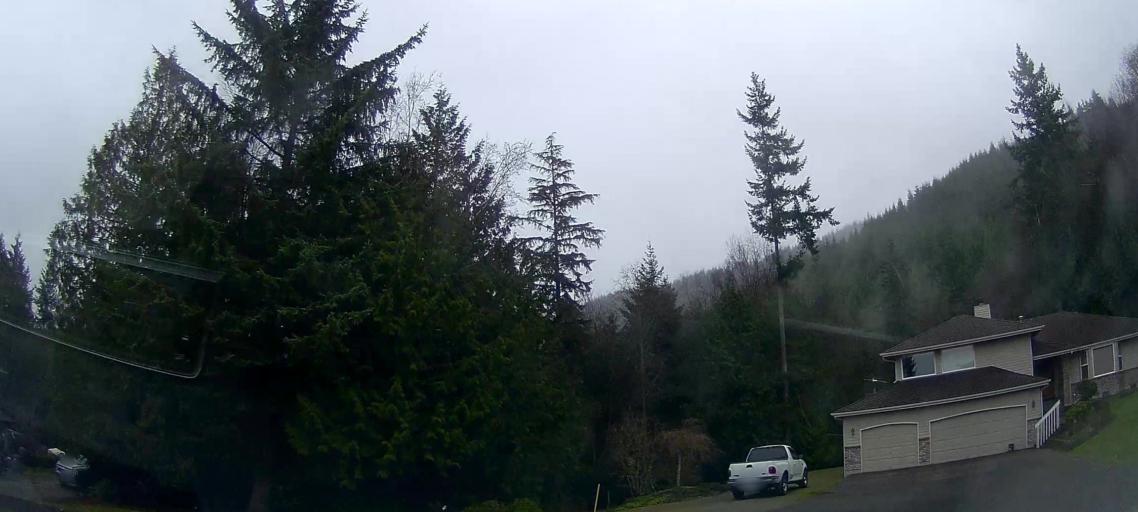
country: US
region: Washington
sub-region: Skagit County
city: Big Lake
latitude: 48.3725
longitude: -122.2940
